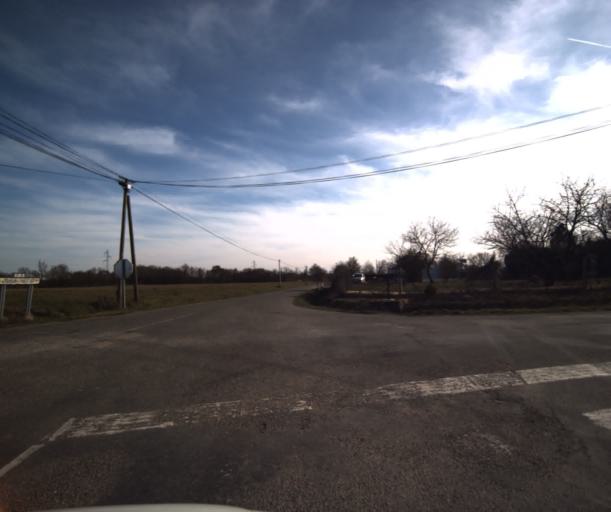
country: FR
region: Midi-Pyrenees
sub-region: Departement du Tarn-et-Garonne
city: Campsas
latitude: 43.9118
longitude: 1.3306
